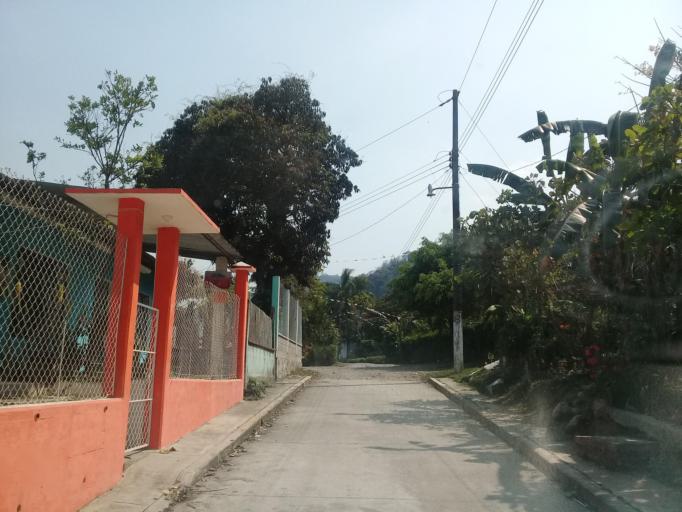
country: MX
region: Veracruz
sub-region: Ixtaczoquitlan
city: Campo Chico
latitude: 18.8282
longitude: -97.0223
